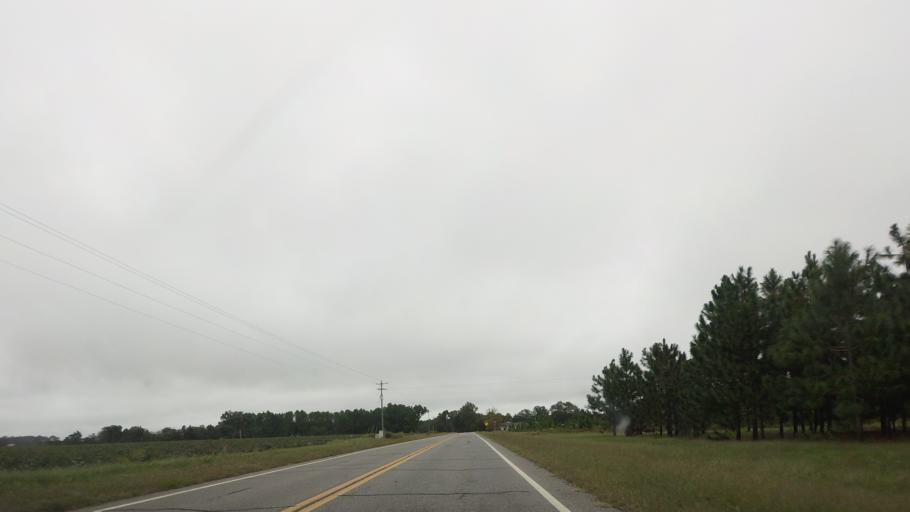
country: US
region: Georgia
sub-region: Irwin County
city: Ocilla
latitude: 31.5080
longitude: -83.2389
